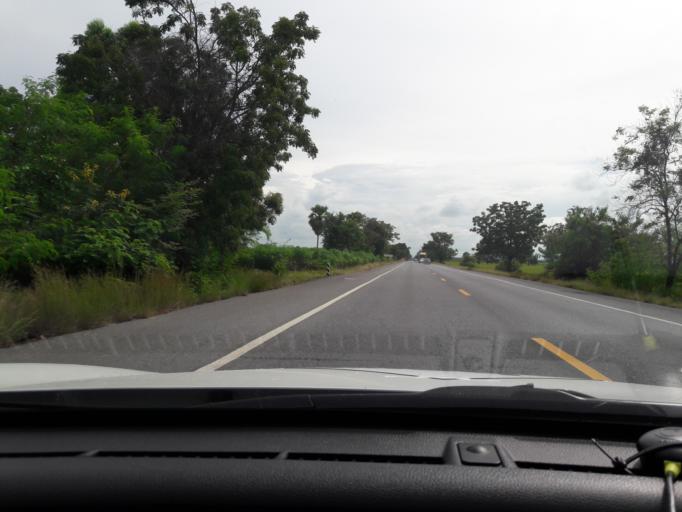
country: TH
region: Nakhon Sawan
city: Phai Sali
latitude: 15.5270
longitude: 100.5484
